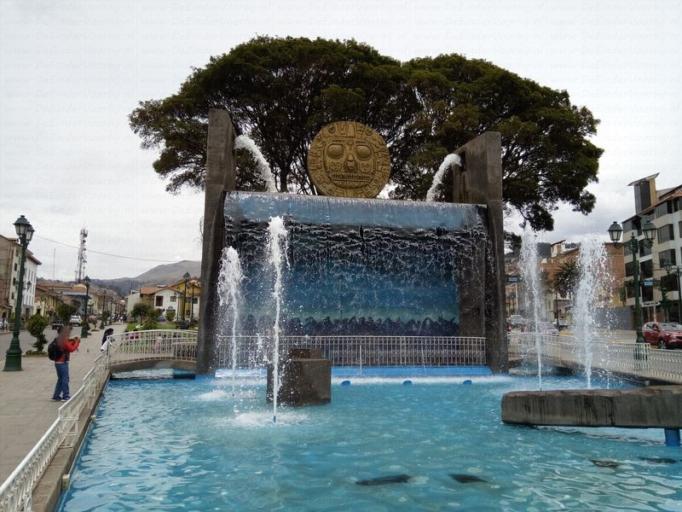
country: PE
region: Cusco
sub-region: Provincia de Cusco
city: Cusco
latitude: -13.5247
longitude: -71.9727
